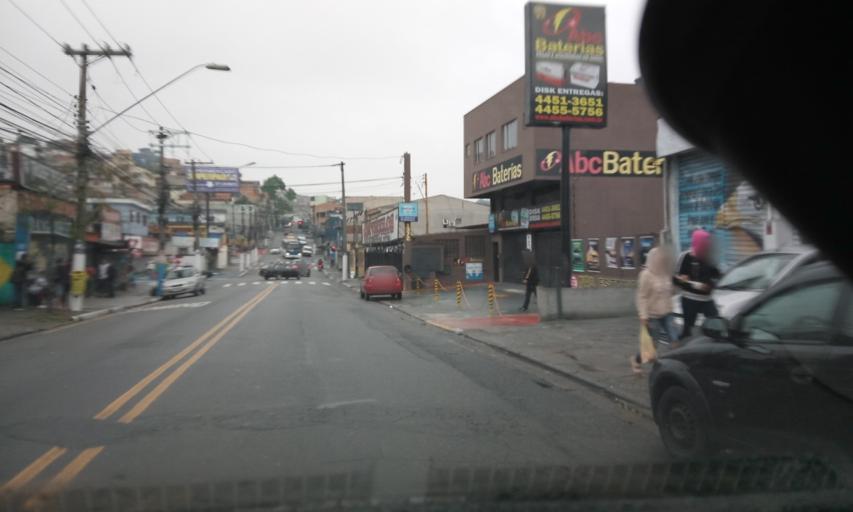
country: BR
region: Sao Paulo
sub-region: Santo Andre
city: Santo Andre
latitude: -23.7014
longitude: -46.5118
